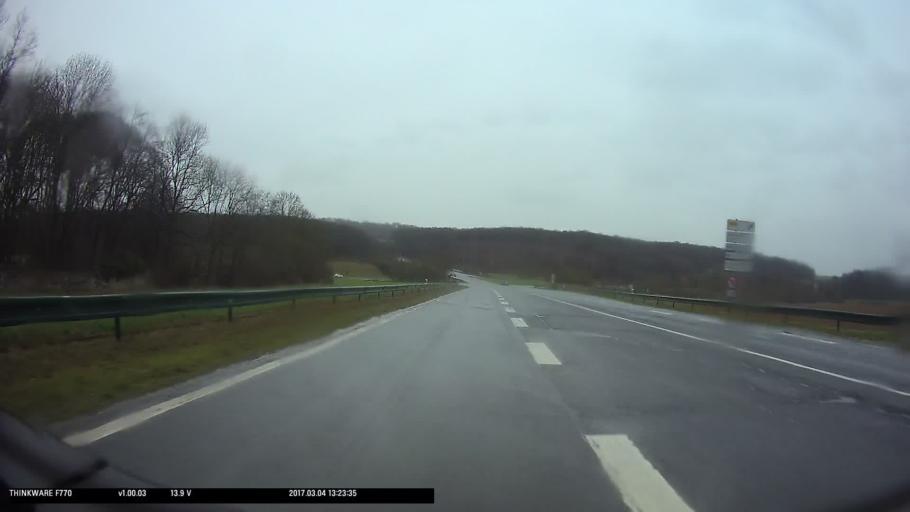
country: FR
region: Ile-de-France
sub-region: Departement du Val-d'Oise
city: Marines
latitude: 49.1335
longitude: 1.9788
